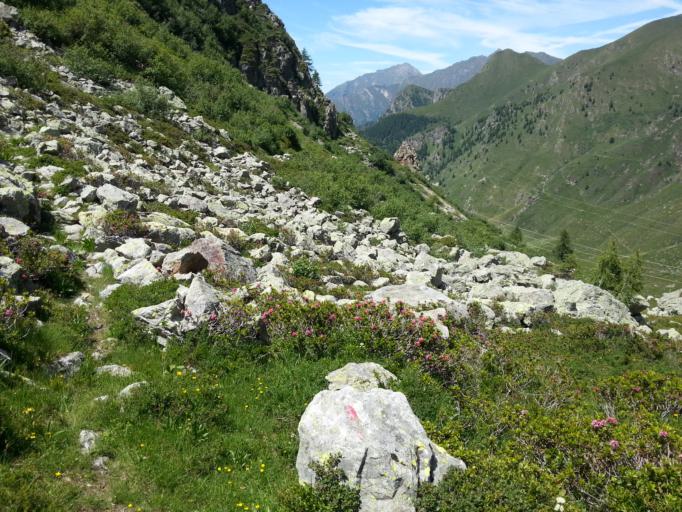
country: IT
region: Lombardy
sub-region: Provincia di Sondrio
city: Gerola Alta
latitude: 46.0261
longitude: 9.5080
